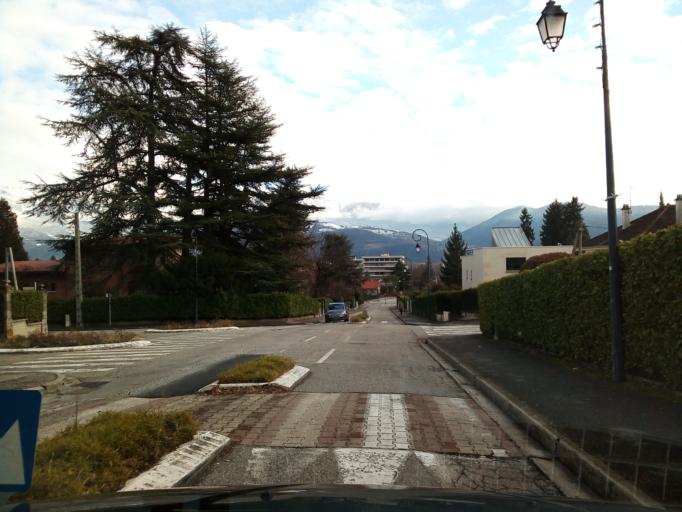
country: FR
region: Rhone-Alpes
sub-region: Departement de l'Isere
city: Corenc
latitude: 45.2087
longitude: 5.7542
